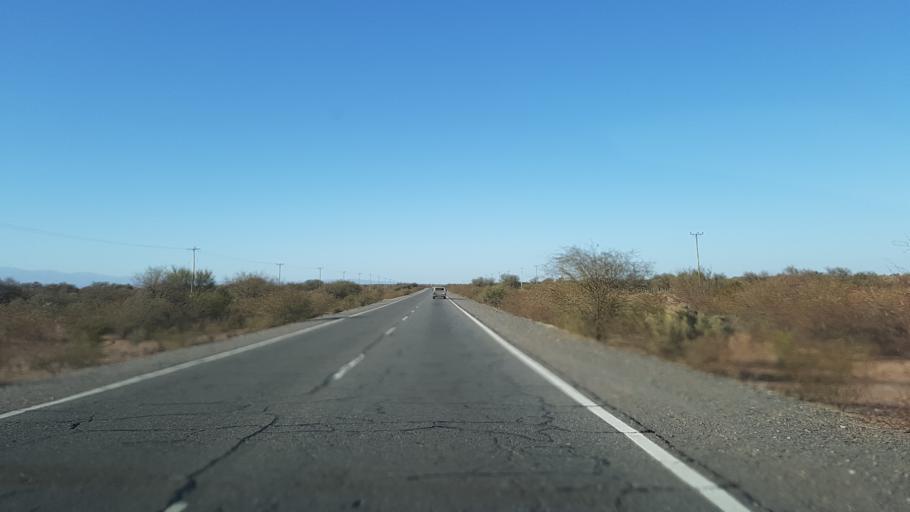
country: AR
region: San Juan
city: Caucete
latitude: -31.6034
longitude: -67.7069
